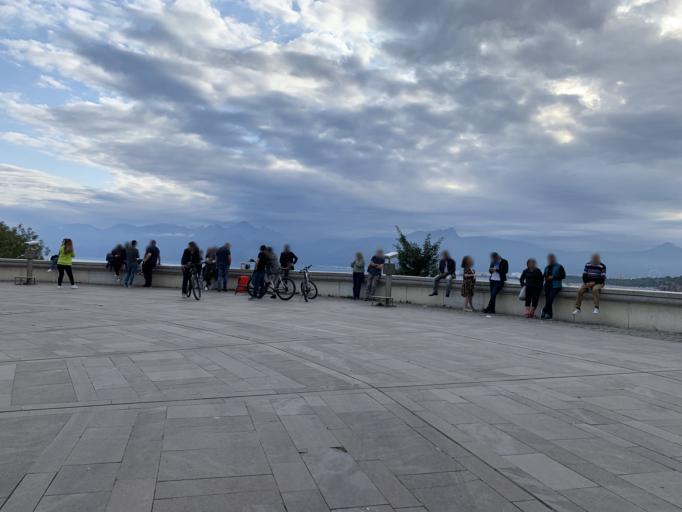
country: TR
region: Antalya
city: Antalya
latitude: 36.8807
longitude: 30.7039
